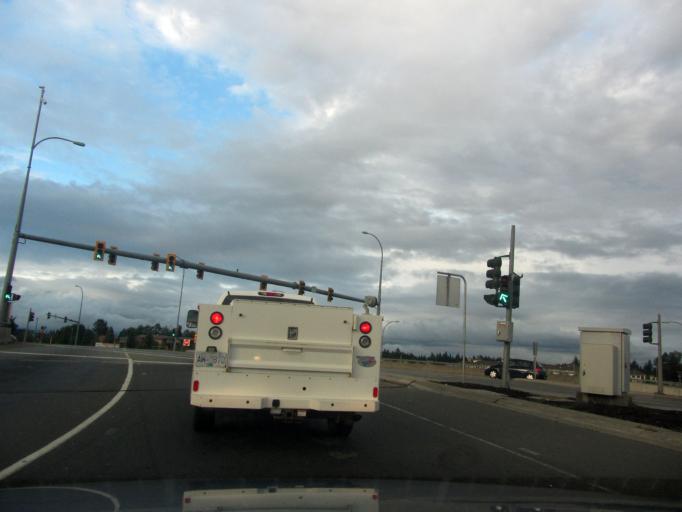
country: CA
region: British Columbia
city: Walnut Grove
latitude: 49.1640
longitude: -122.6694
